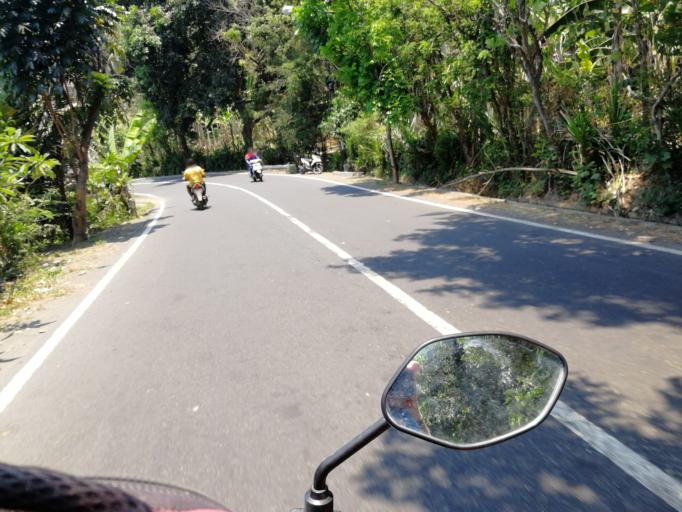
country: ID
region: Bali
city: Padangbai
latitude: -8.5233
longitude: 115.5015
